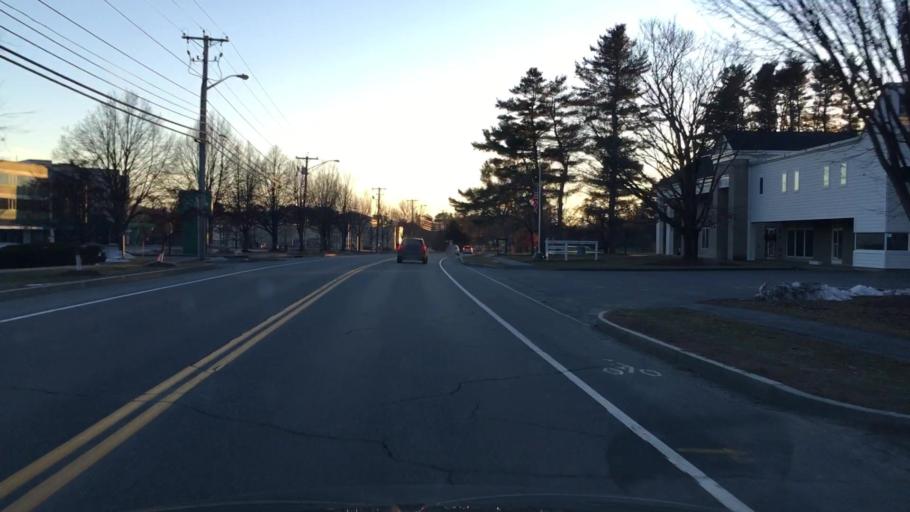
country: US
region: New Hampshire
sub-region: Grafton County
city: Hanover
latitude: 43.7200
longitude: -72.2727
